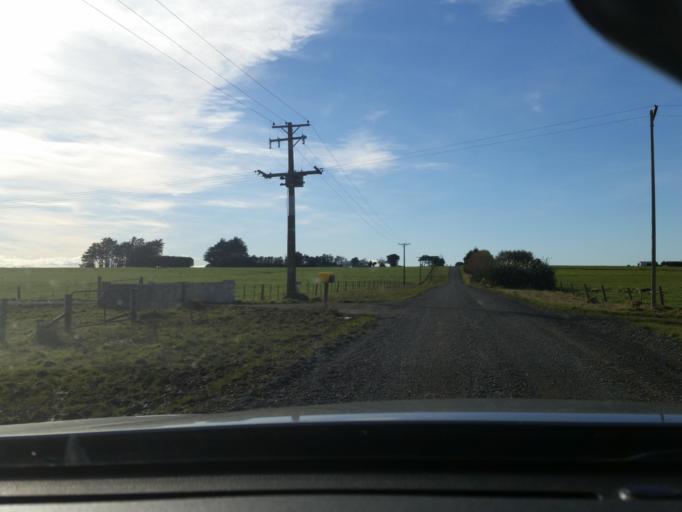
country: NZ
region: Southland
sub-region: Southland District
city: Riverton
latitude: -46.2987
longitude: 168.0390
